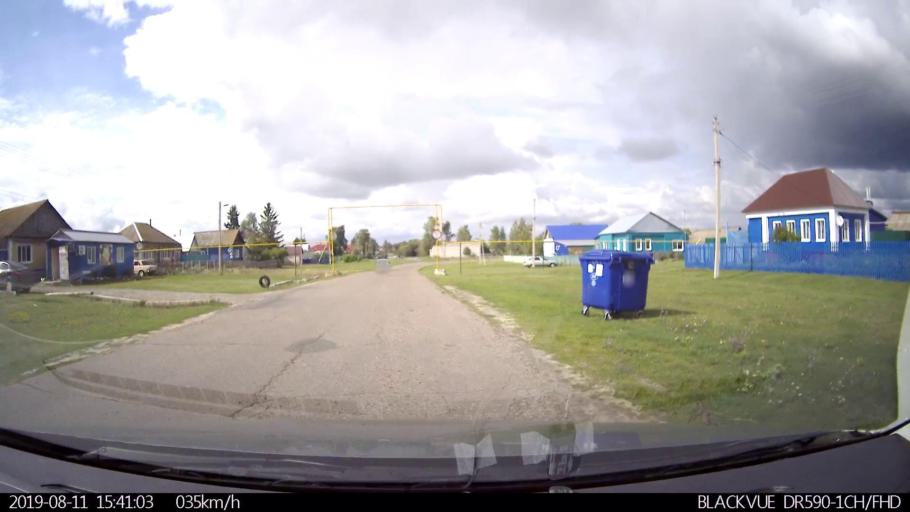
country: RU
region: Ulyanovsk
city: Ignatovka
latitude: 53.8724
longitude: 47.6489
